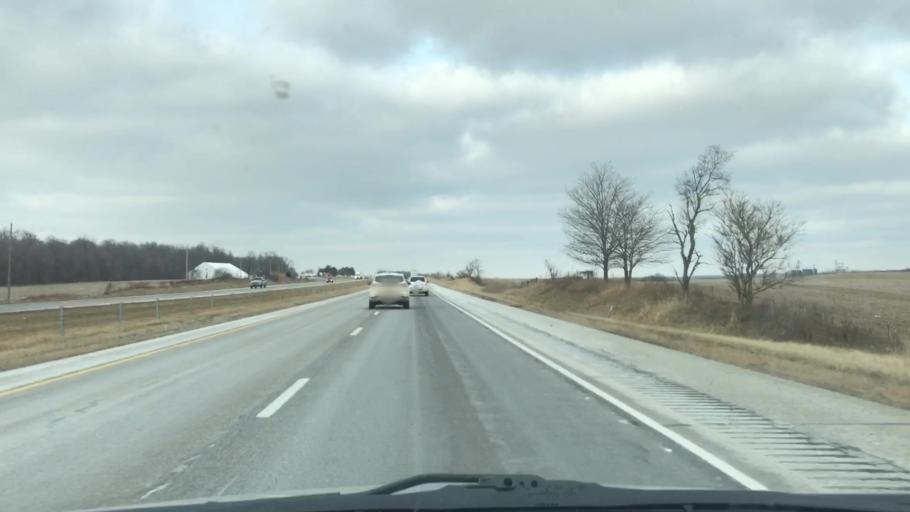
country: US
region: Indiana
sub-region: Steuben County
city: Angola
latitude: 41.5738
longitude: -85.0580
